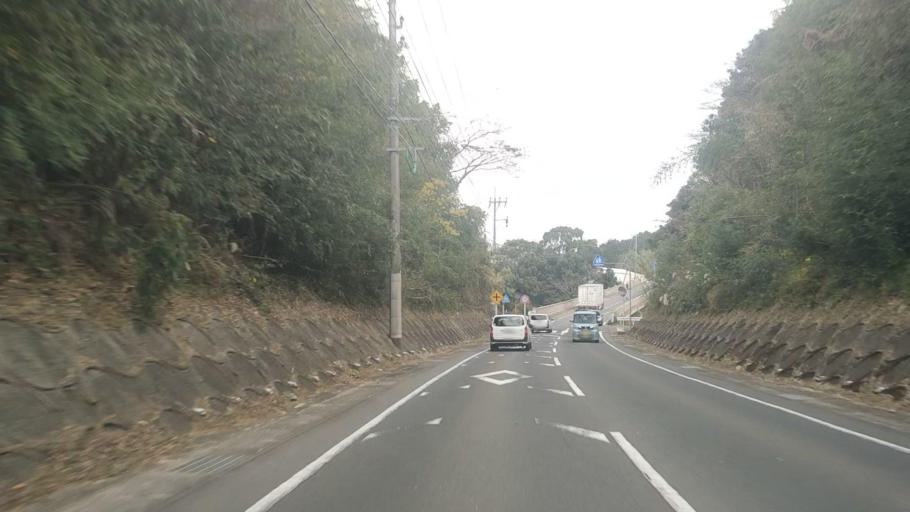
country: JP
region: Nagasaki
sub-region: Isahaya-shi
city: Isahaya
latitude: 32.8138
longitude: 130.1726
